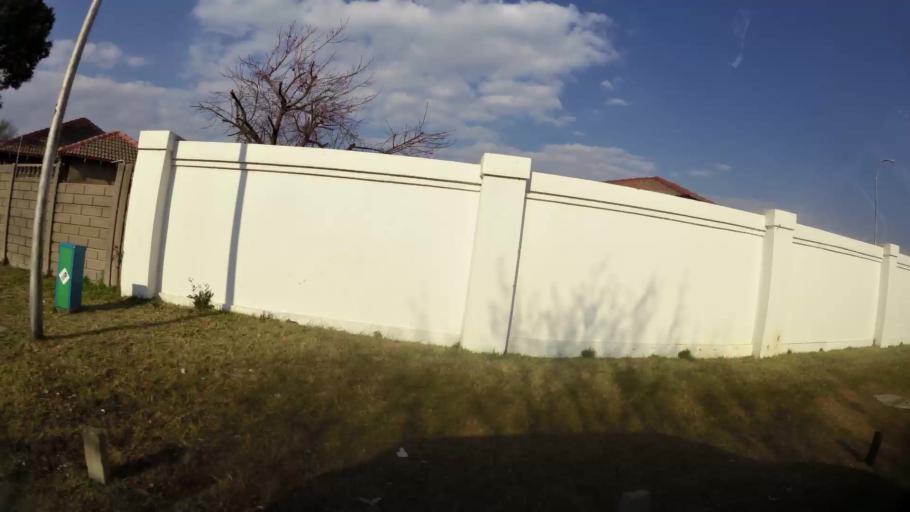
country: ZA
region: Gauteng
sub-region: Ekurhuleni Metropolitan Municipality
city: Benoni
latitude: -26.1248
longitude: 28.3655
